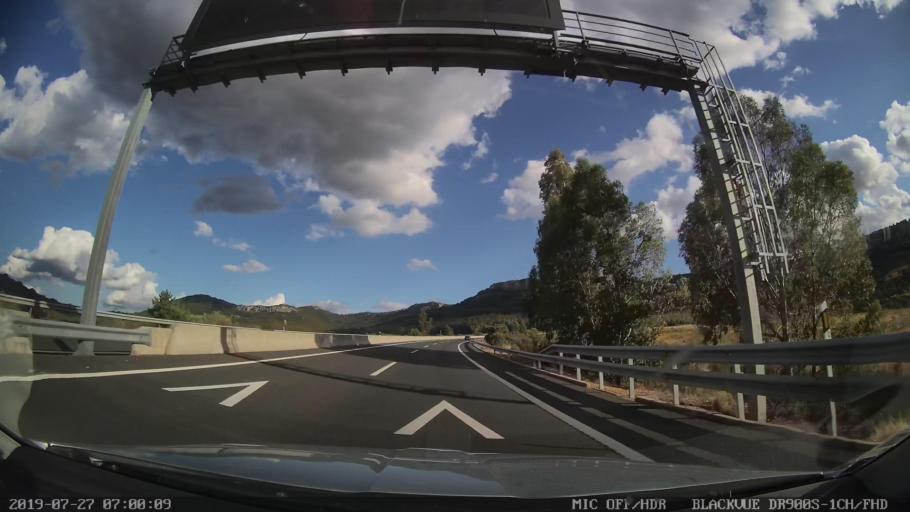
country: ES
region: Extremadura
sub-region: Provincia de Caceres
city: Higuera
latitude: 39.7062
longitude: -5.6900
